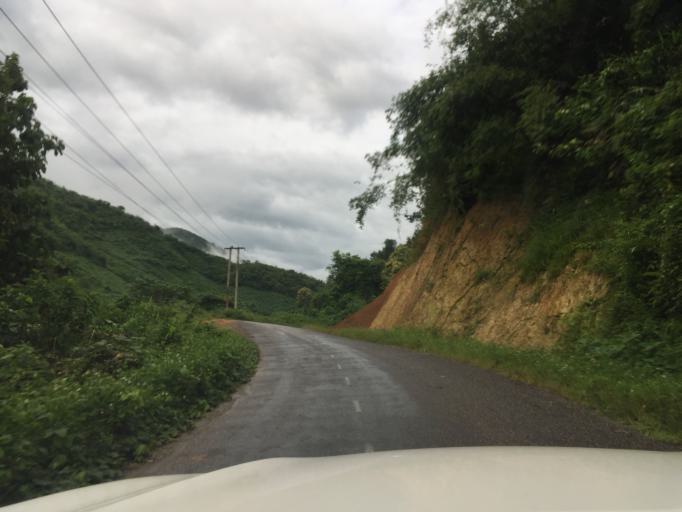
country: LA
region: Oudomxai
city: Muang La
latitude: 21.0400
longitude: 102.2410
